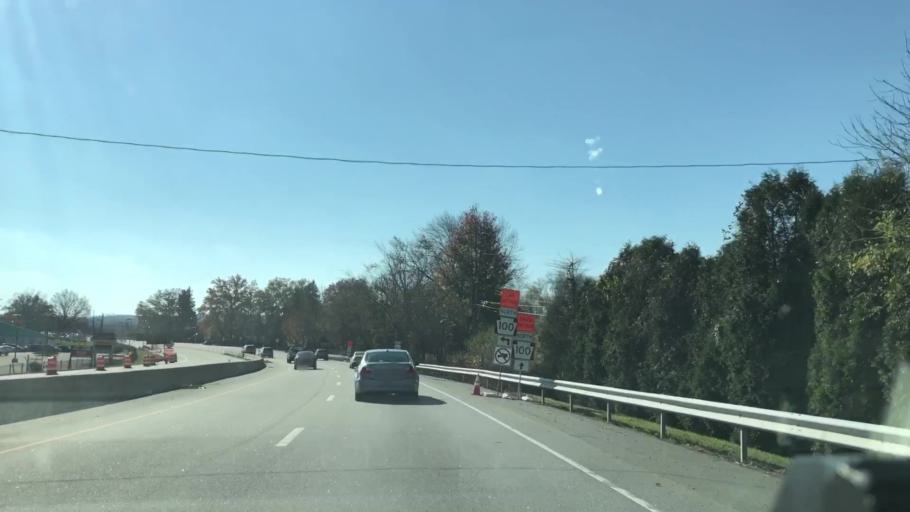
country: US
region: Pennsylvania
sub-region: Montgomery County
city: Pottstown
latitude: 40.2518
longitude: -75.6612
